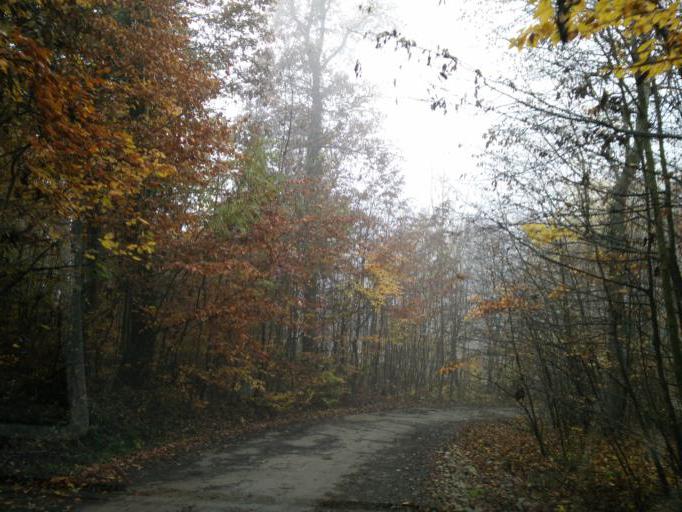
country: DE
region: Baden-Wuerttemberg
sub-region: Tuebingen Region
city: Tuebingen
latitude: 48.5406
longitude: 8.9833
